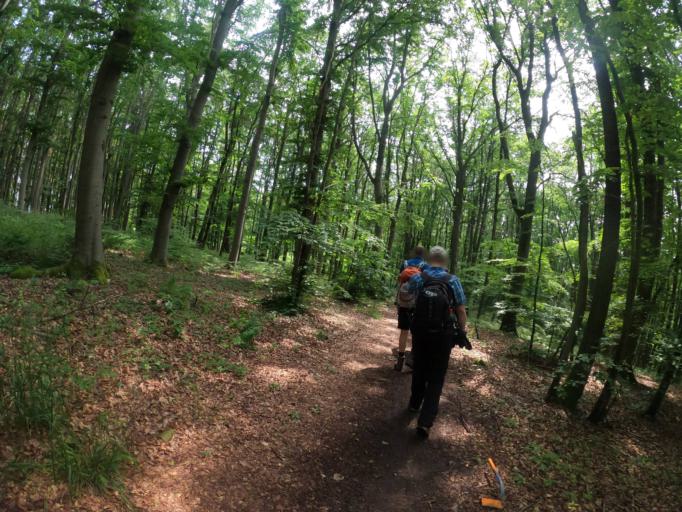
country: DE
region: Bavaria
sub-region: Upper Franconia
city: Litzendorf
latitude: 49.9270
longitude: 11.0553
